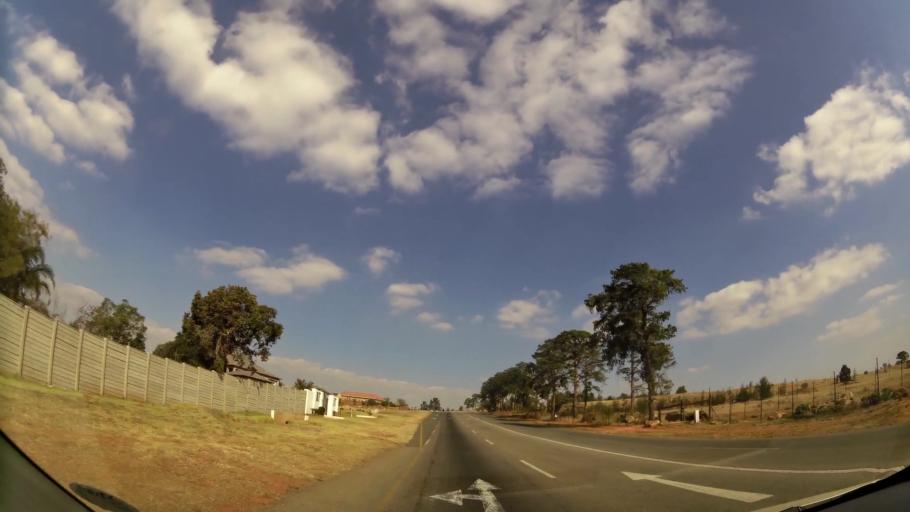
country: ZA
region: Gauteng
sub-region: West Rand District Municipality
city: Krugersdorp
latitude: -26.0531
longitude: 27.7542
